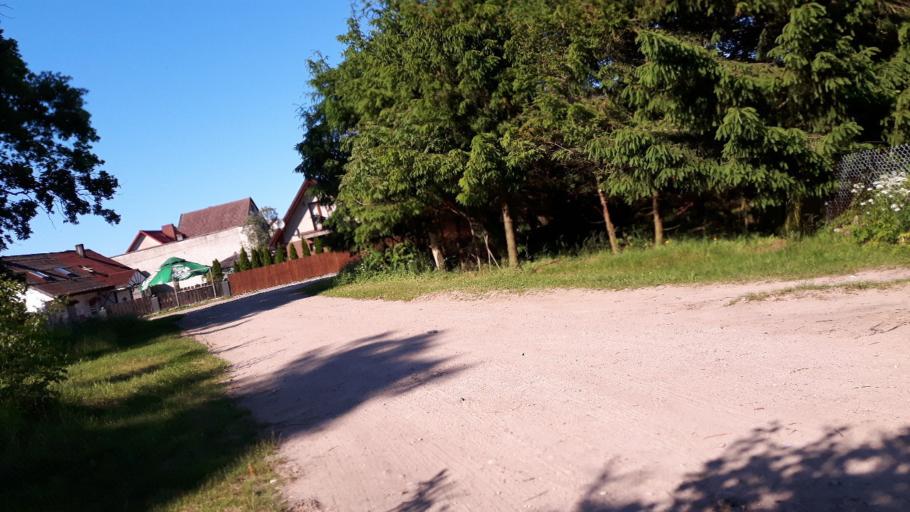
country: PL
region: Pomeranian Voivodeship
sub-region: Powiat leborski
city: Leba
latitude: 54.7206
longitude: 17.5243
